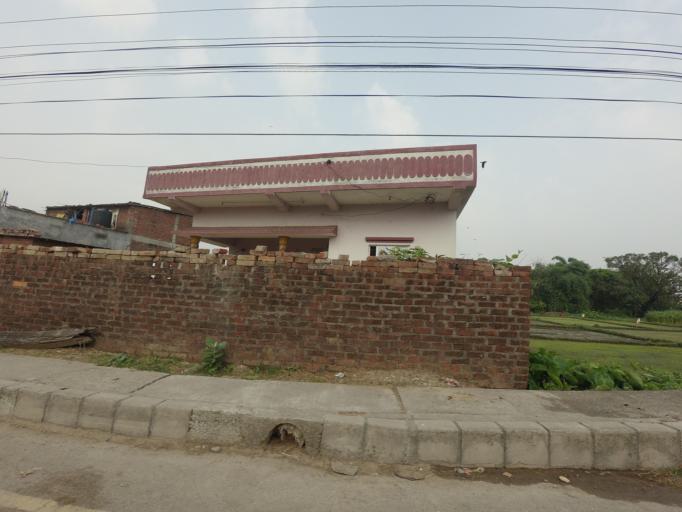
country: NP
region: Western Region
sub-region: Lumbini Zone
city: Bhairahawa
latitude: 27.4955
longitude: 83.4495
